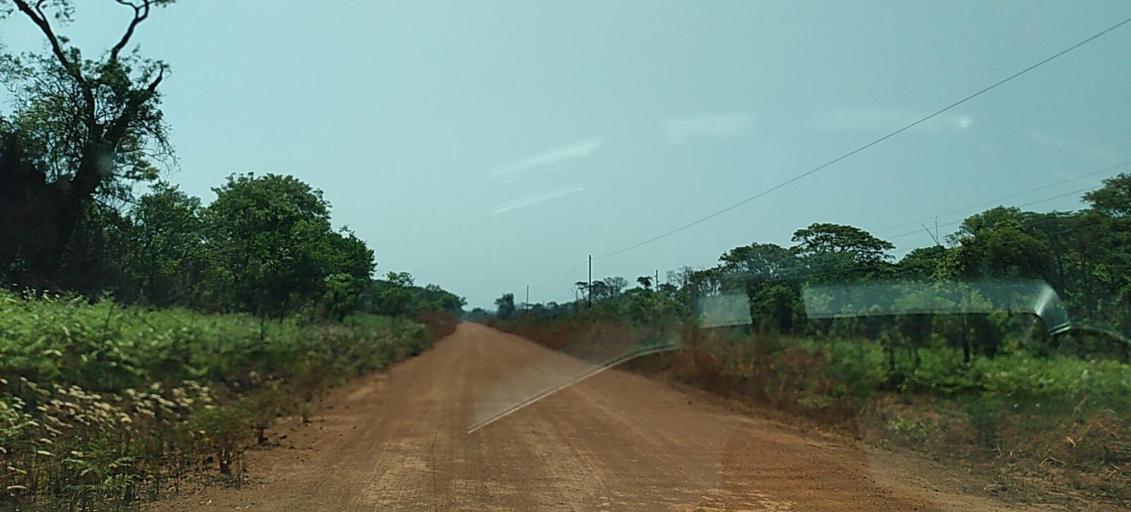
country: ZM
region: North-Western
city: Kansanshi
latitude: -11.9955
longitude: 26.6514
